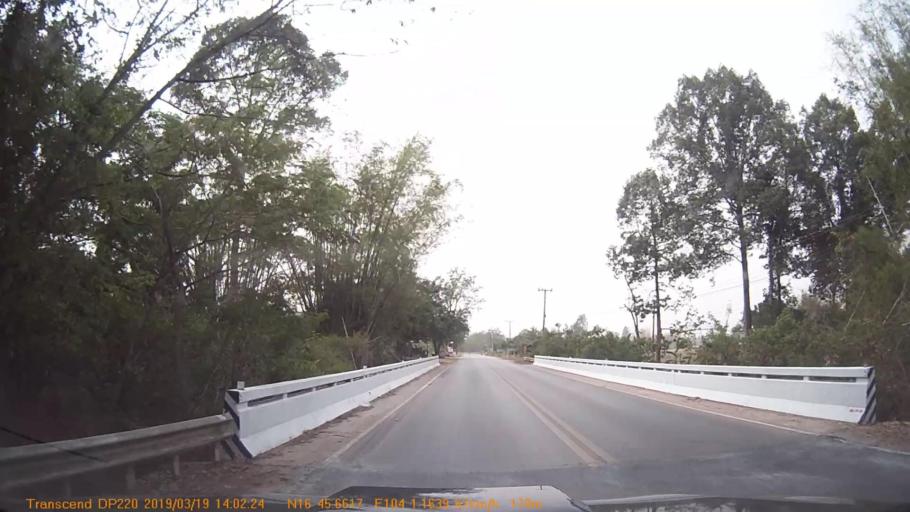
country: TH
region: Kalasin
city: Na Khu
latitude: 16.7611
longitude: 104.0191
